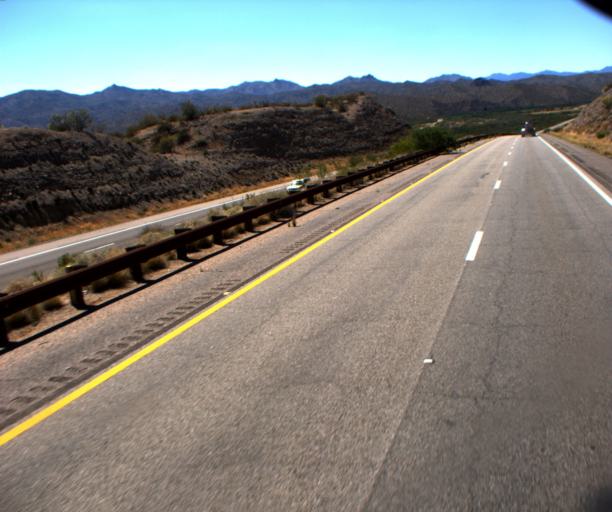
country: US
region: Arizona
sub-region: Yavapai County
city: Bagdad
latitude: 34.6352
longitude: -113.5535
